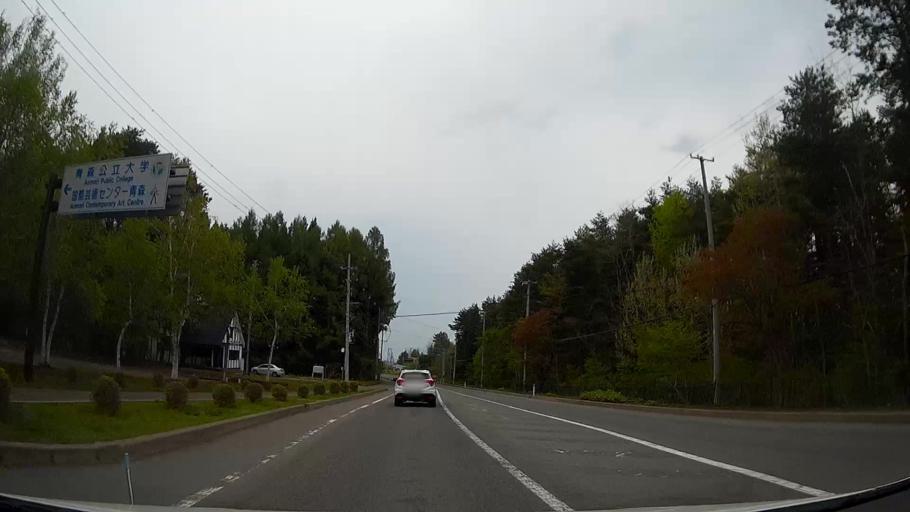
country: JP
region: Aomori
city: Aomori Shi
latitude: 40.7542
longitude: 140.7758
